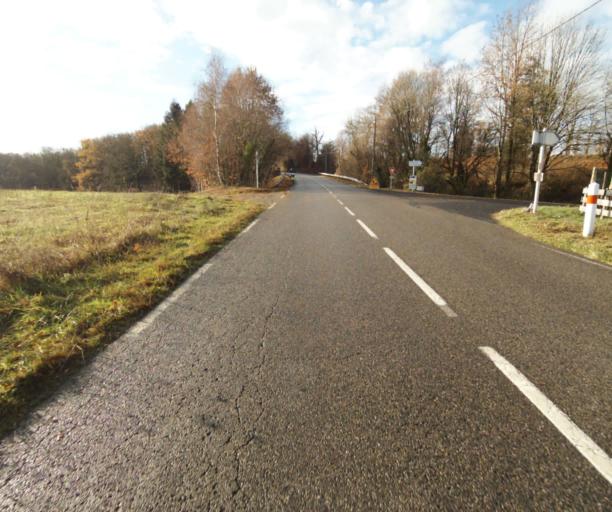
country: FR
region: Limousin
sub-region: Departement de la Correze
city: Saint-Mexant
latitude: 45.2518
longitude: 1.6307
